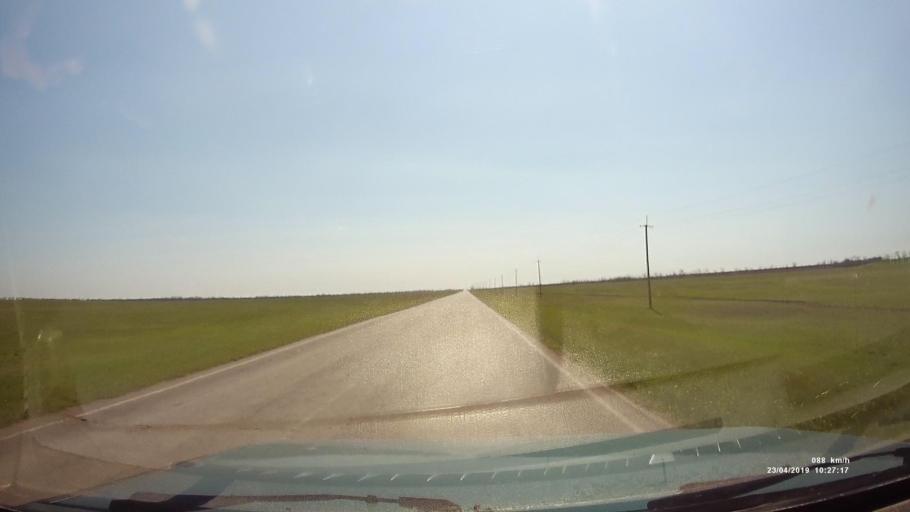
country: RU
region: Kalmykiya
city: Yashalta
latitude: 46.6150
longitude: 42.4886
